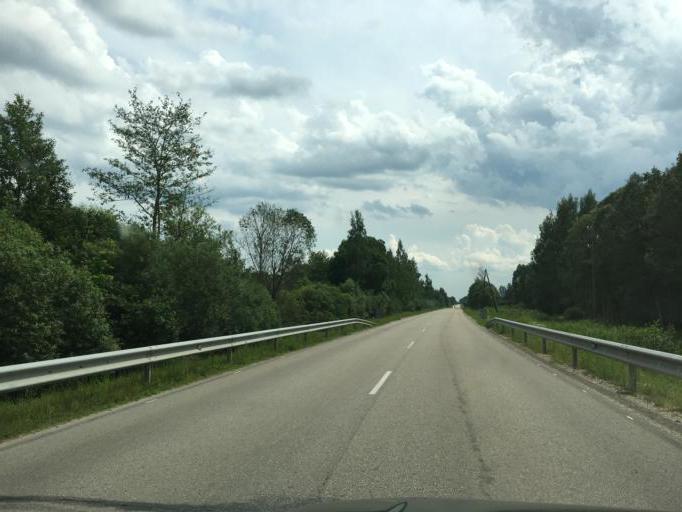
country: LV
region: Rugaju
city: Rugaji
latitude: 56.9710
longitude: 27.0655
